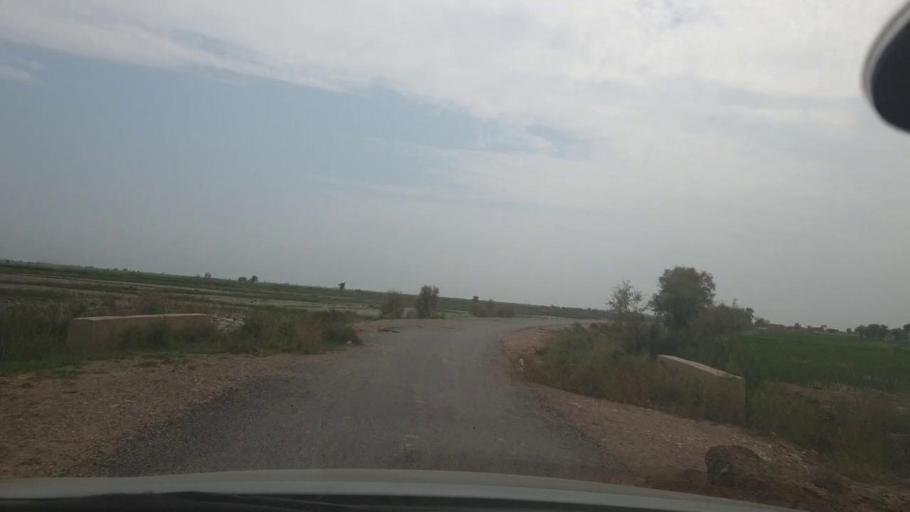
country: PK
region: Balochistan
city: Garhi Khairo
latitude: 28.0222
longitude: 68.0445
